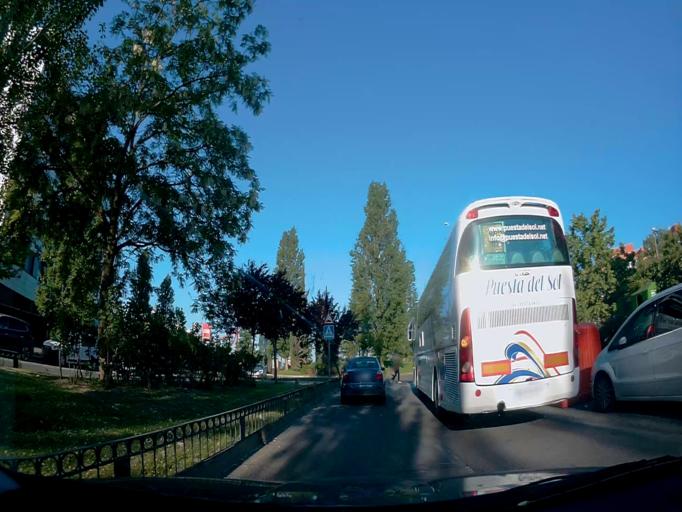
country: ES
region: Madrid
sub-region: Provincia de Madrid
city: Alcorcon
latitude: 40.3422
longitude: -3.8460
